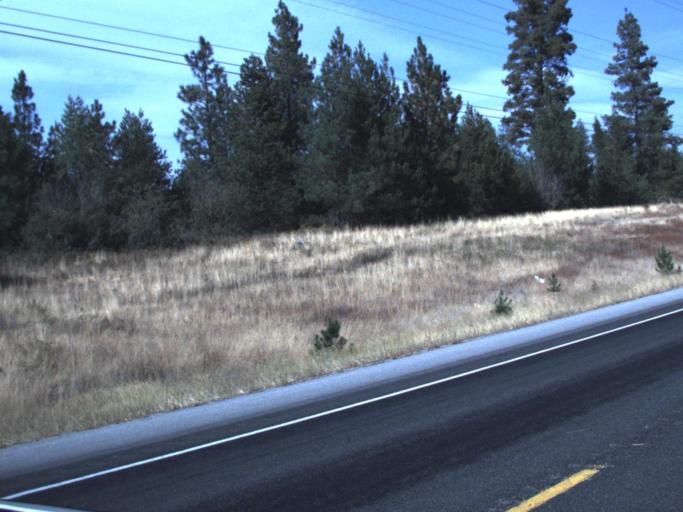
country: US
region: Washington
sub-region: Pend Oreille County
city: Newport
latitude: 48.1026
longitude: -117.2464
